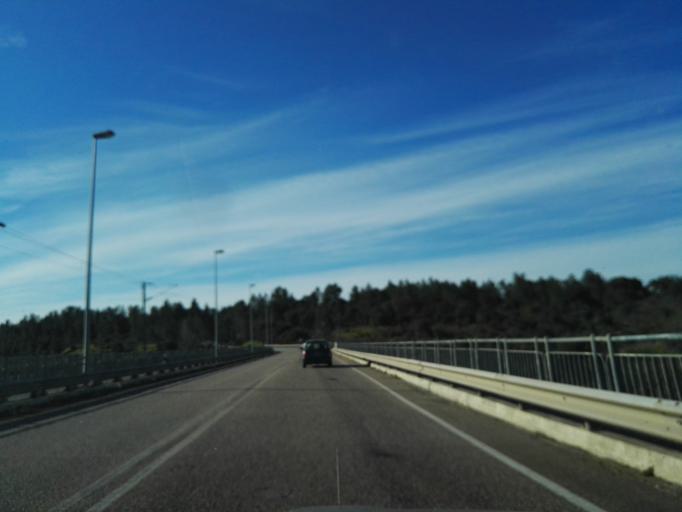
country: PT
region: Santarem
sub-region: Abrantes
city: Alferrarede
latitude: 39.4715
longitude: -8.0665
